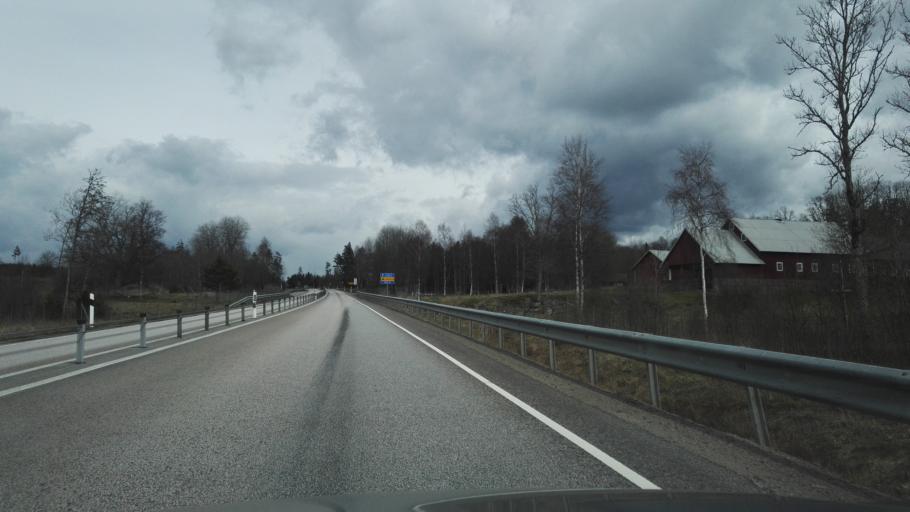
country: SE
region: Kronoberg
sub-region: Vaxjo Kommun
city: Braas
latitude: 56.9991
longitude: 15.0232
